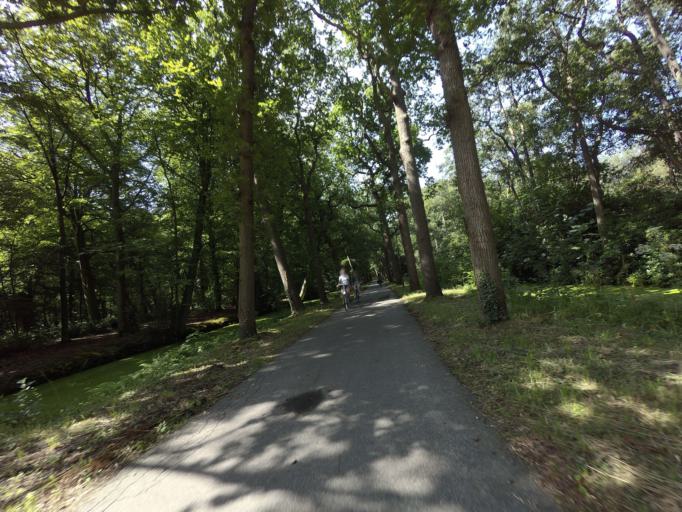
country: NL
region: South Holland
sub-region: Gemeente Leidschendam-Voorburg
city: Voorburg
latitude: 52.1004
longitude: 4.3387
